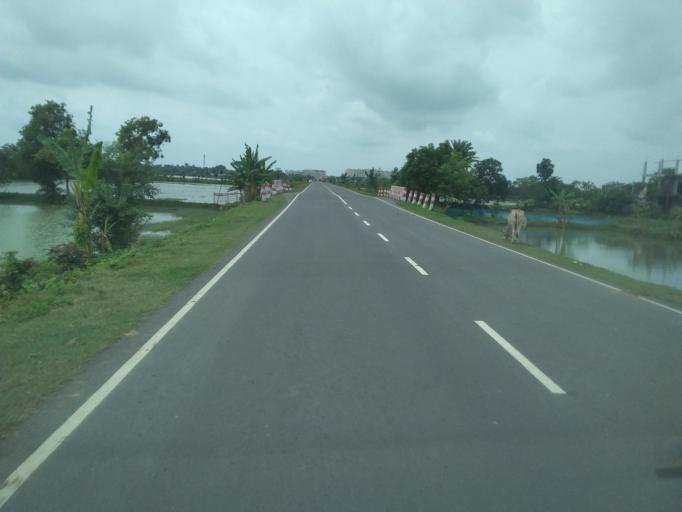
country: BD
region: Khulna
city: Satkhira
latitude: 22.7009
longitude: 89.0536
